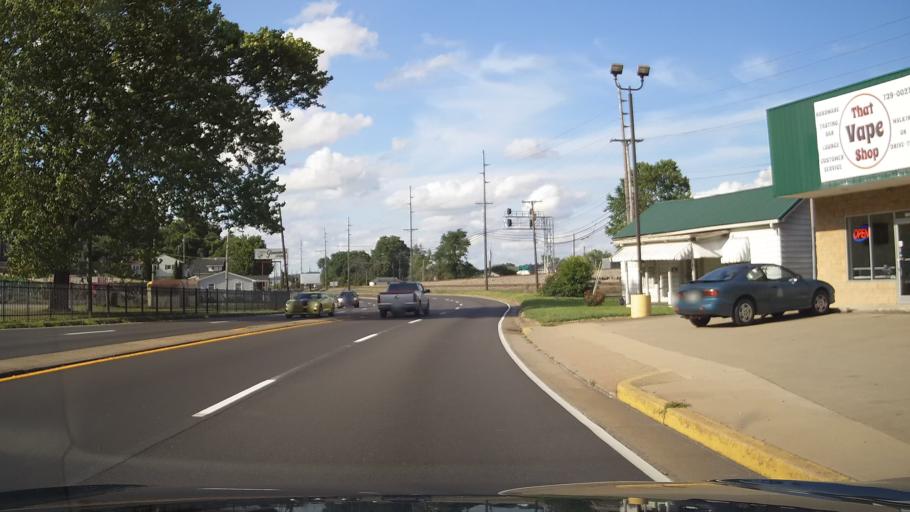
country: US
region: Kentucky
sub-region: Boyd County
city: Catlettsburg
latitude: 38.4066
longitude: -82.6005
